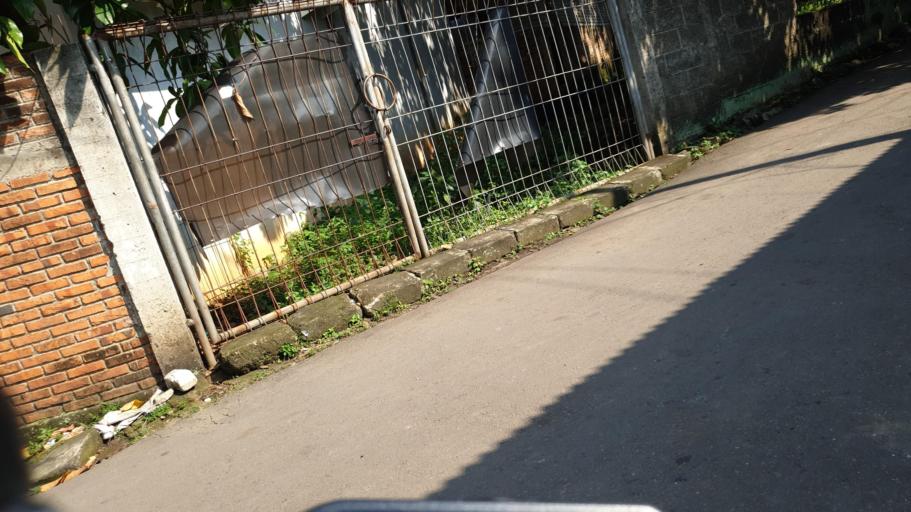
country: ID
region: West Java
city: Depok
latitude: -6.3276
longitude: 106.8261
